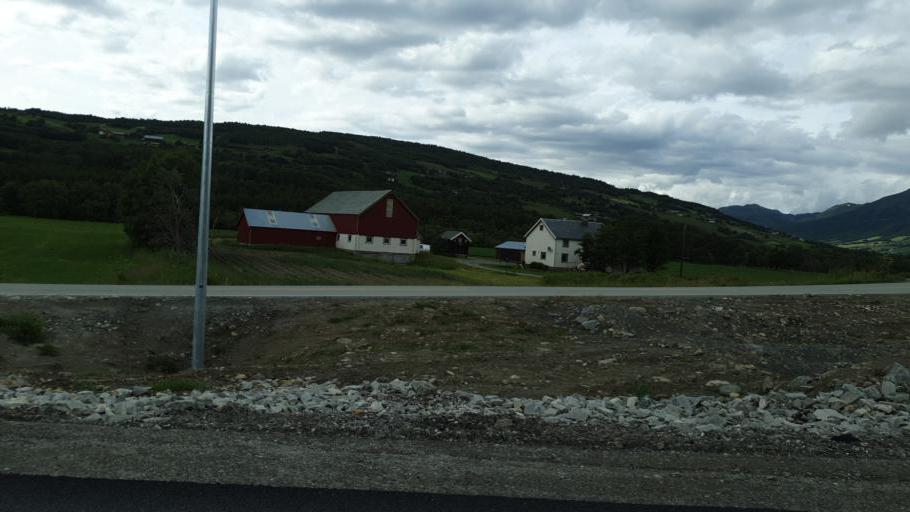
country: NO
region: Sor-Trondelag
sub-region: Oppdal
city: Oppdal
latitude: 62.5619
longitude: 9.6421
